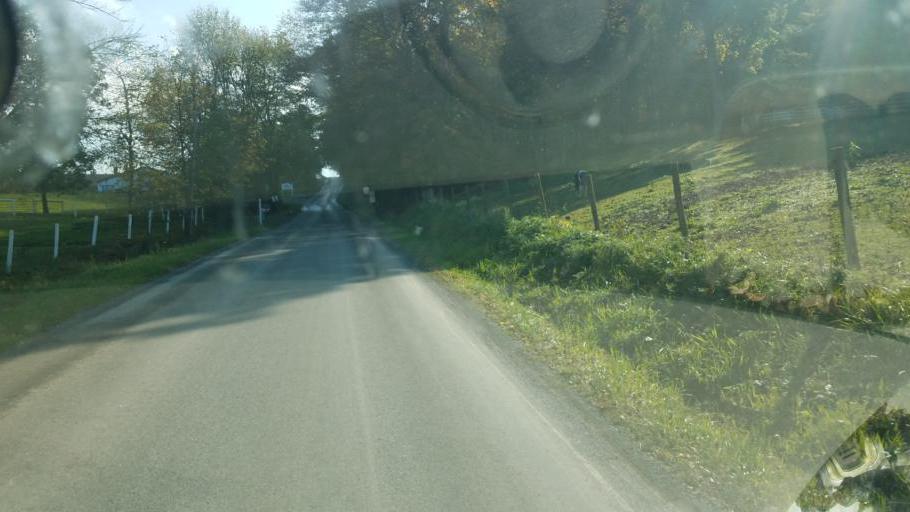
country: US
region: Ohio
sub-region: Wayne County
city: Apple Creek
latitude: 40.6682
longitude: -81.8420
